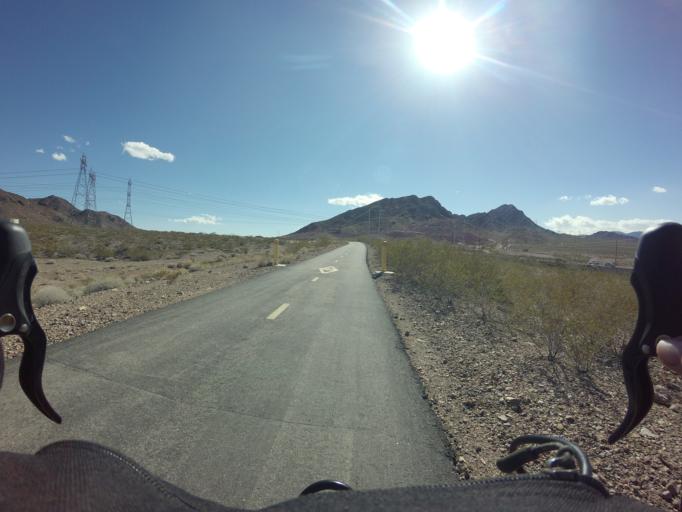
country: US
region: Nevada
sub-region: Clark County
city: Henderson
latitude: 35.9870
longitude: -114.9205
